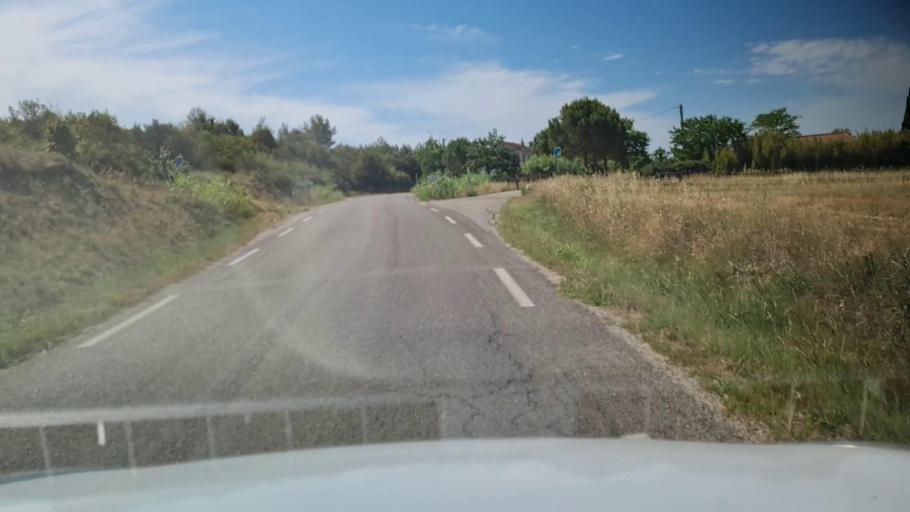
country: FR
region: Languedoc-Roussillon
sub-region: Departement du Gard
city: Nages-et-Solorgues
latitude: 43.7969
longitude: 4.2159
